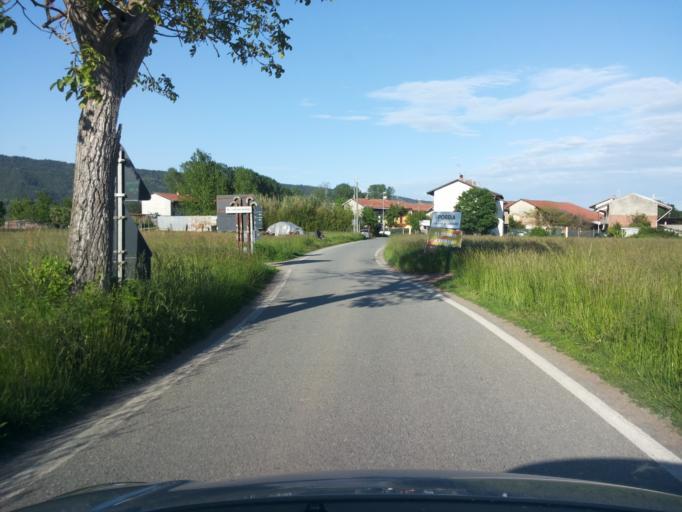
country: IT
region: Piedmont
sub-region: Provincia di Torino
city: Albiano d'Ivrea
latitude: 45.4419
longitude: 7.9633
